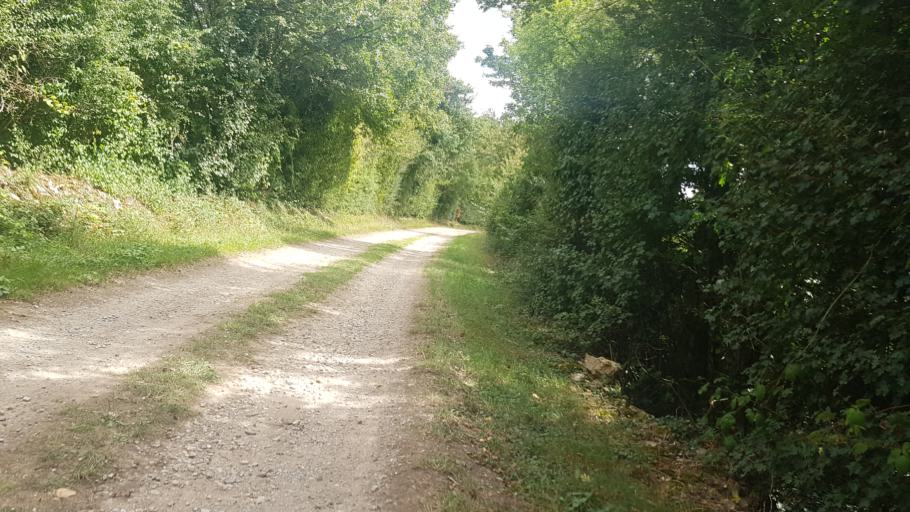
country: FR
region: Poitou-Charentes
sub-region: Departement des Deux-Sevres
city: Vouille
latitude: 46.3174
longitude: -0.3441
